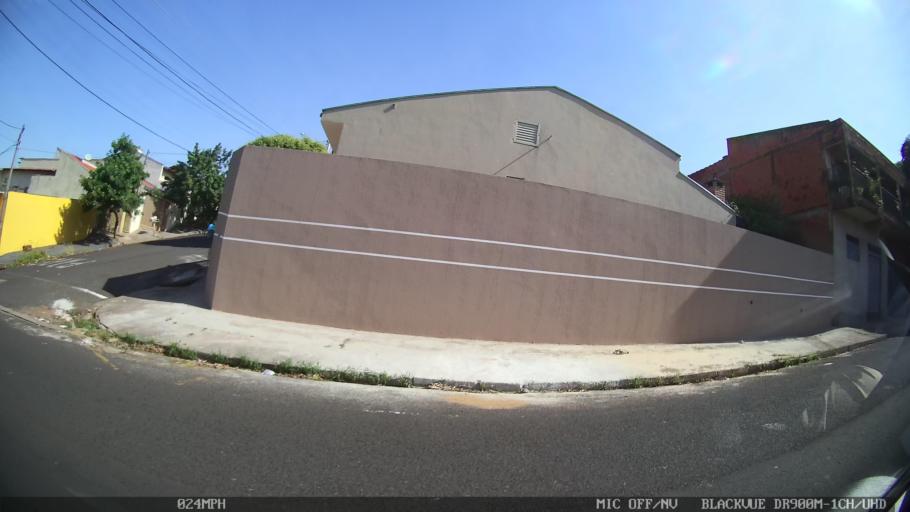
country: BR
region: Sao Paulo
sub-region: Sao Jose Do Rio Preto
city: Sao Jose do Rio Preto
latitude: -20.7900
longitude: -49.4277
